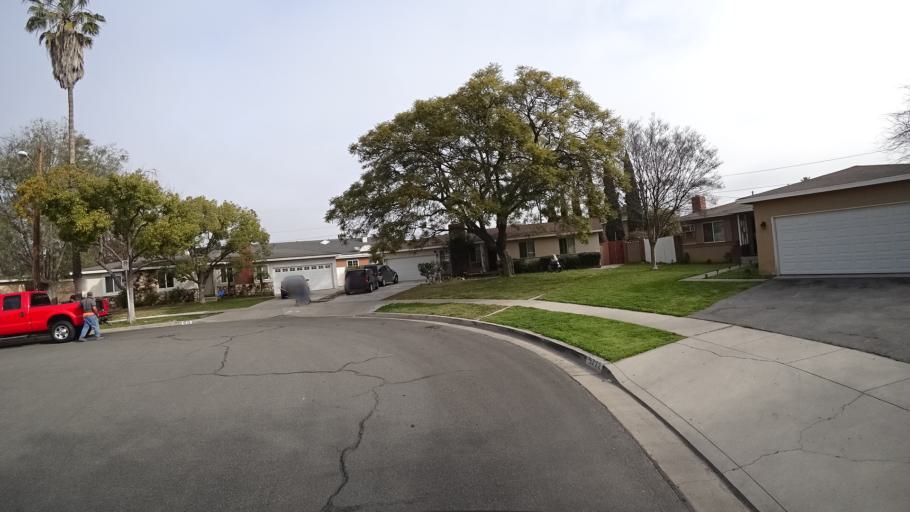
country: US
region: California
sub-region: Orange County
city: Stanton
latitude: 33.8165
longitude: -117.9899
